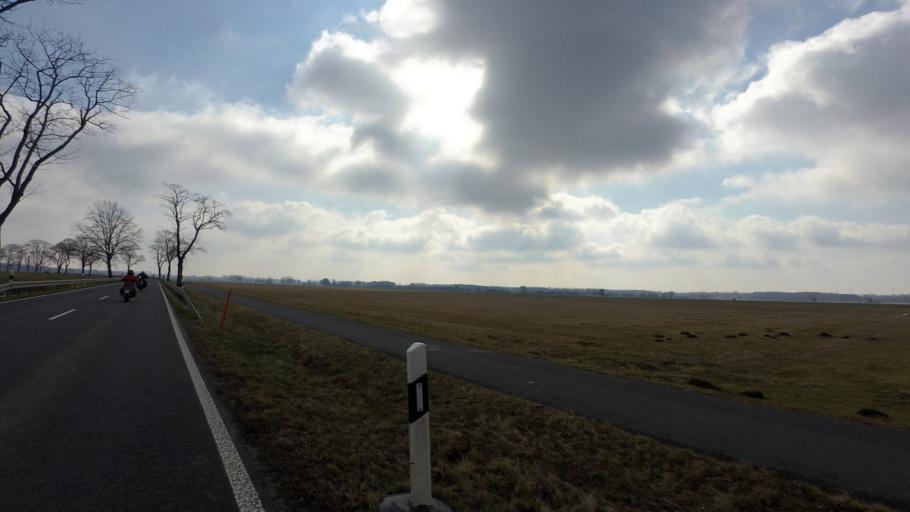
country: DE
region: Brandenburg
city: Wandlitz
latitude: 52.6790
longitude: 13.4445
